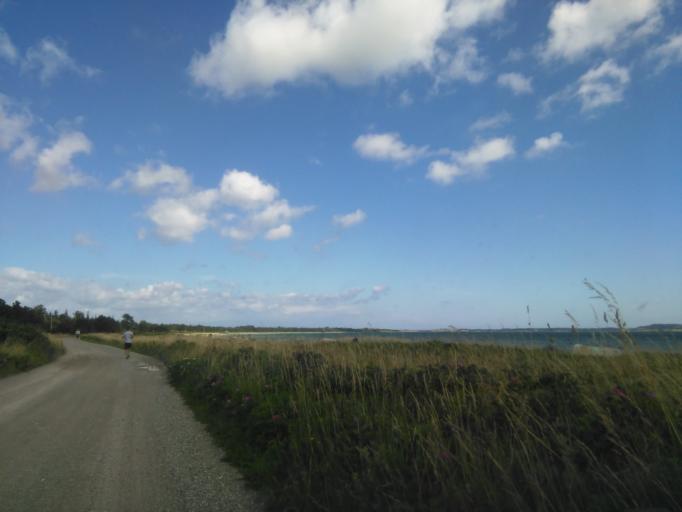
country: DK
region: Central Jutland
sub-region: Syddjurs Kommune
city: Ronde
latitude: 56.1819
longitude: 10.4502
